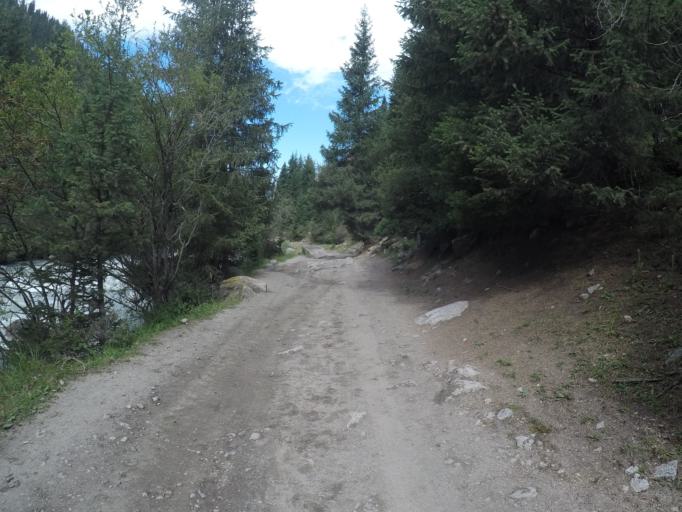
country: KG
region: Ysyk-Koel
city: Teploklyuchenka
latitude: 42.4431
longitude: 78.5517
